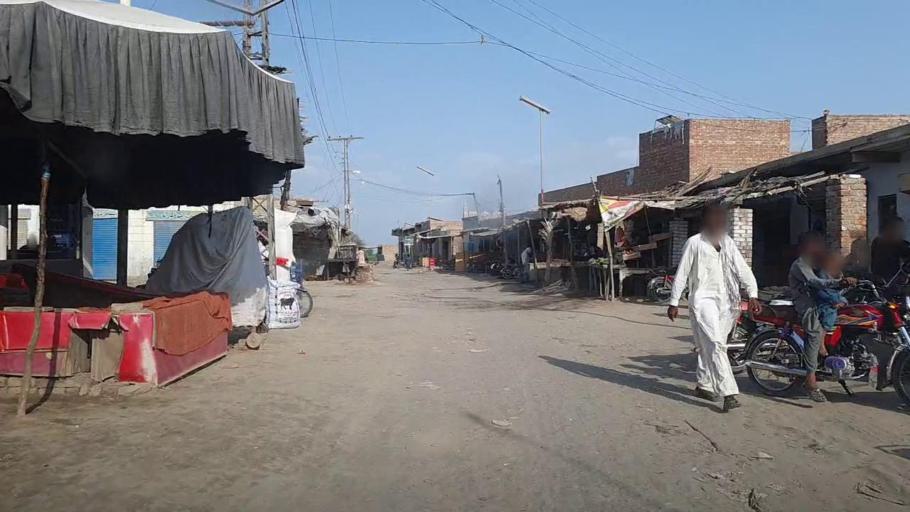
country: PK
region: Sindh
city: Khairpur
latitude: 28.0770
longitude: 69.7957
